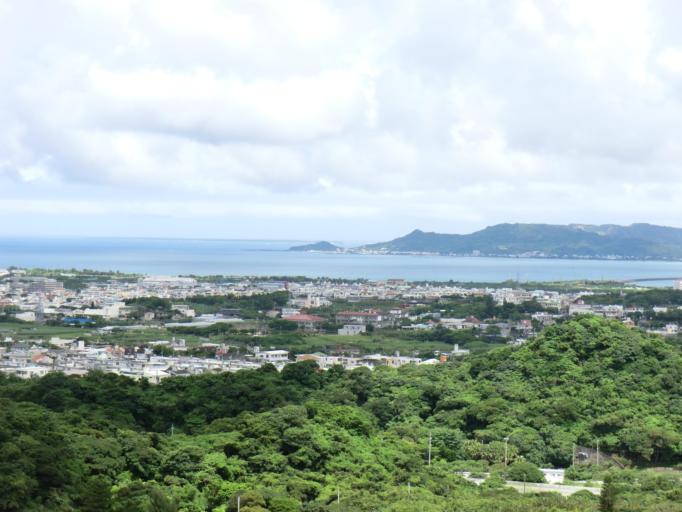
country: JP
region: Okinawa
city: Ginowan
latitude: 26.2269
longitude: 127.7418
